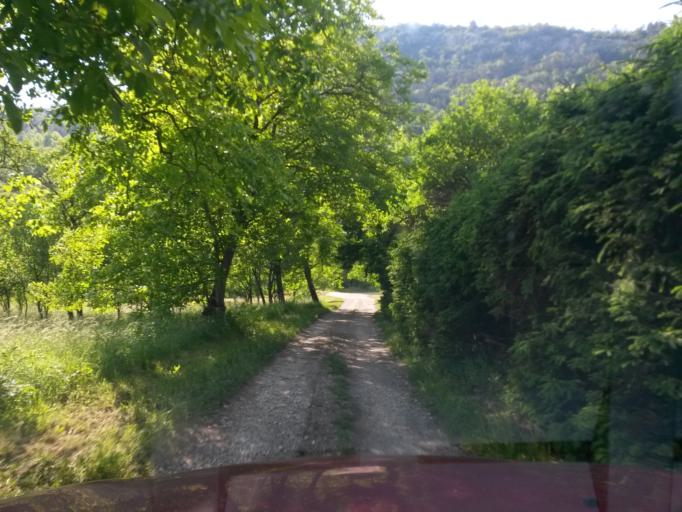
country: SK
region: Kosicky
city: Roznava
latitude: 48.5983
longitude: 20.6444
